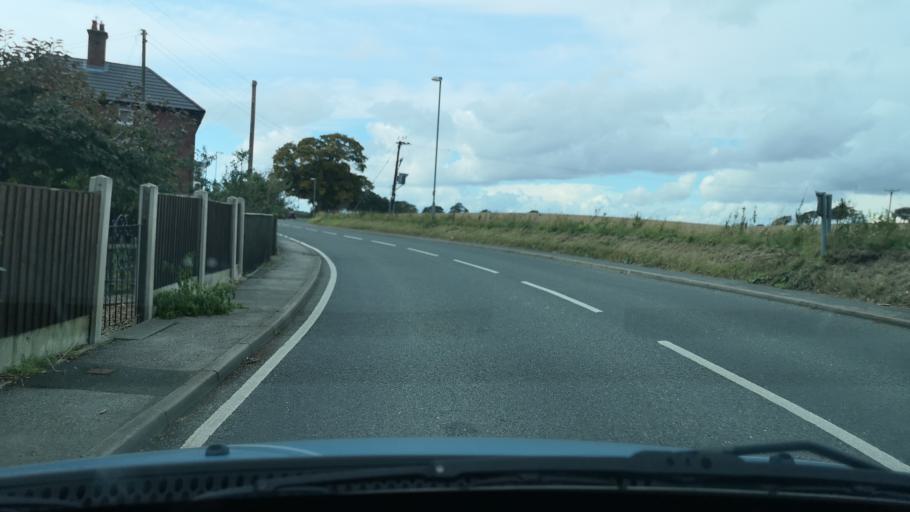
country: GB
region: England
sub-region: City and Borough of Wakefield
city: Low Ackworth
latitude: 53.6607
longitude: -1.3413
